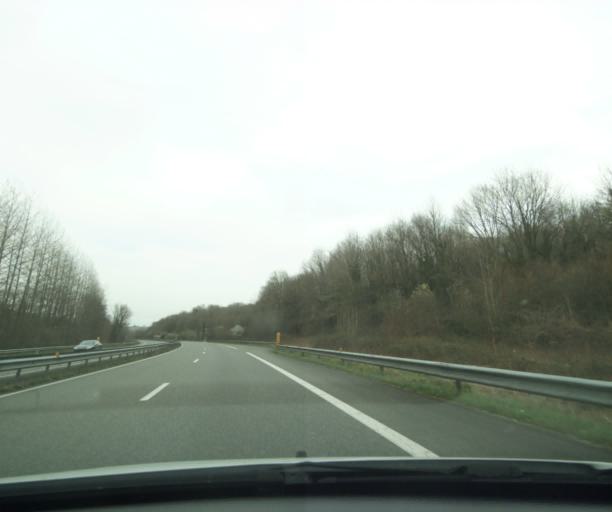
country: FR
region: Aquitaine
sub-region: Departement des Pyrenees-Atlantiques
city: Briscous
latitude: 43.4477
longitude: -1.3173
